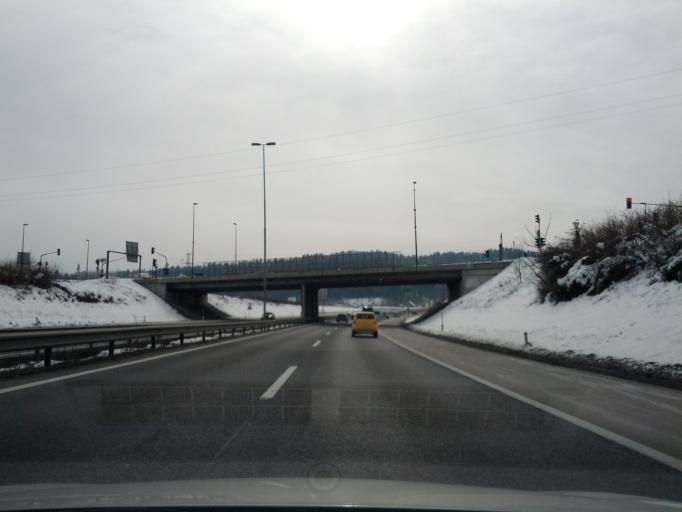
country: SI
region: Skofljica
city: Lavrica
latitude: 46.0447
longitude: 14.5763
